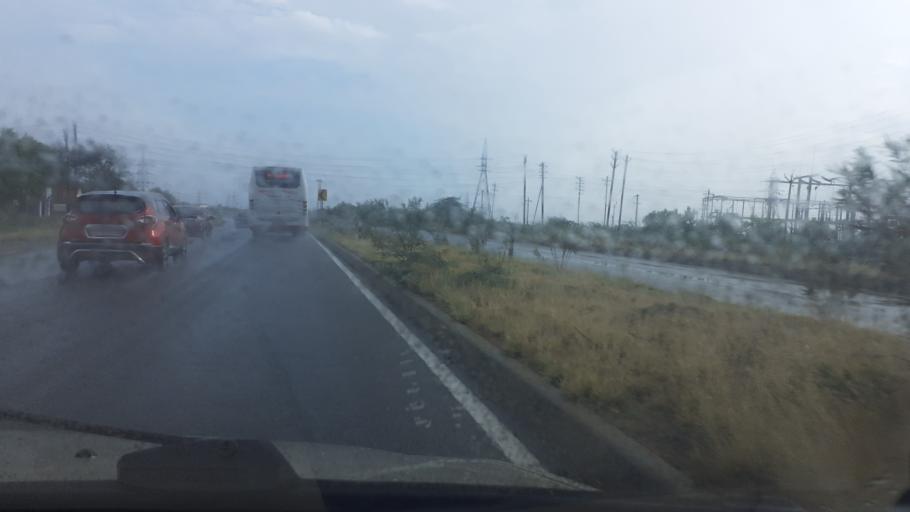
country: IN
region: Tamil Nadu
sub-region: Tirunelveli Kattabo
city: Gangaikondan
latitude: 8.8889
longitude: 77.7681
